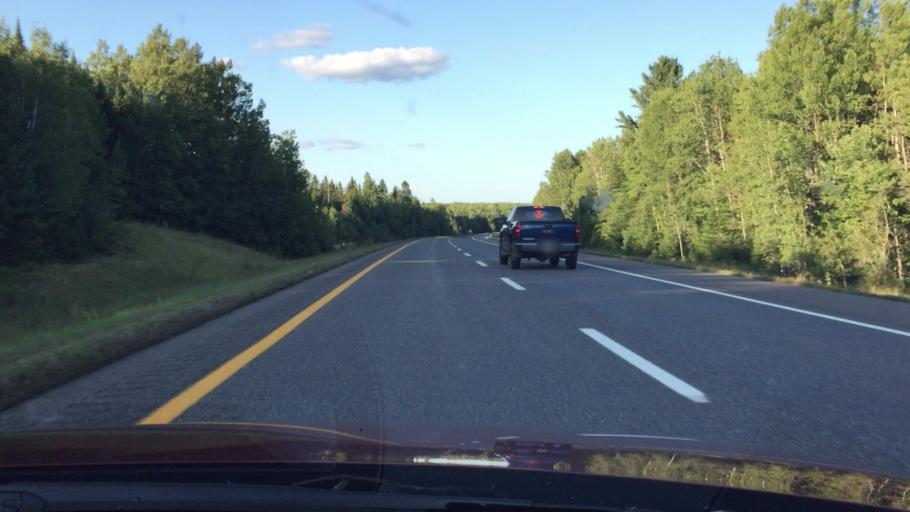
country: US
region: Maine
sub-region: Penobscot County
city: Patten
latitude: 46.0402
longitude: -68.2636
